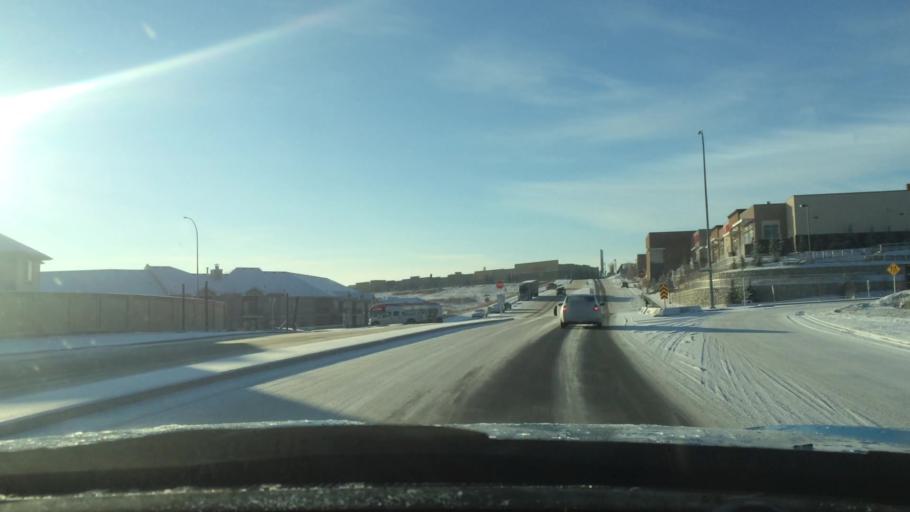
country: CA
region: Alberta
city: Calgary
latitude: 51.1634
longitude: -114.1598
